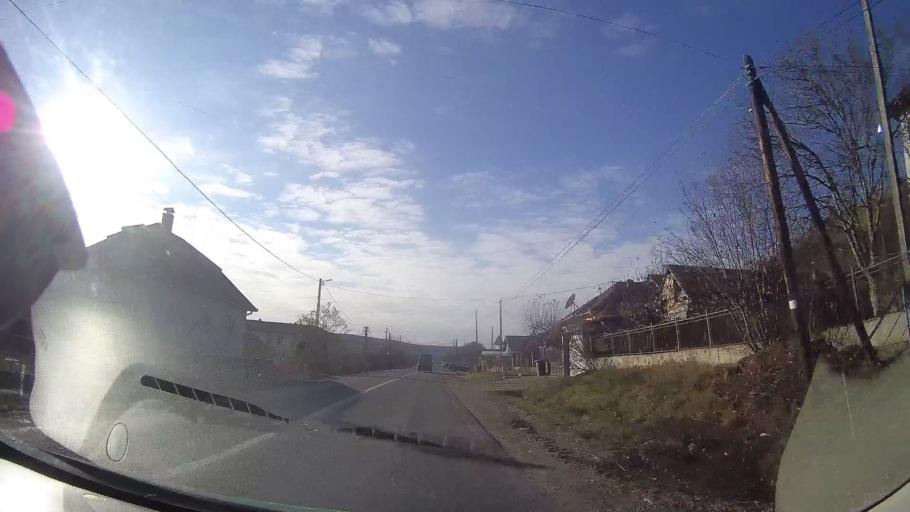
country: RO
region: Cluj
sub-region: Comuna Caianu
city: Caianu
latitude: 46.7973
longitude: 23.9179
